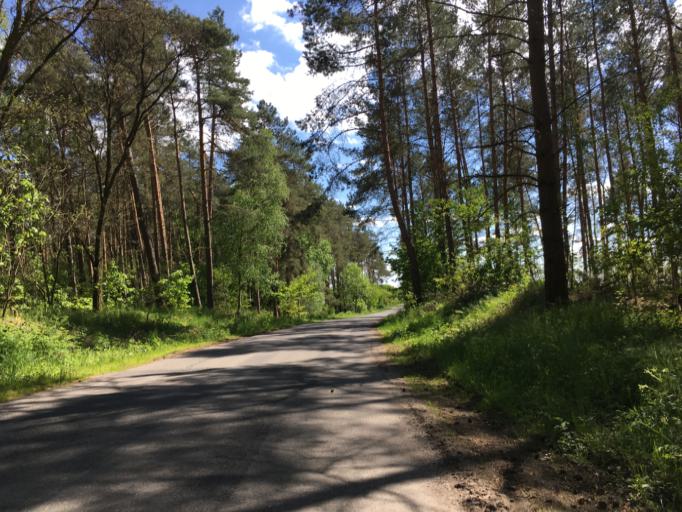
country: DE
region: Brandenburg
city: Rudnitz
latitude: 52.7088
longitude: 13.6609
